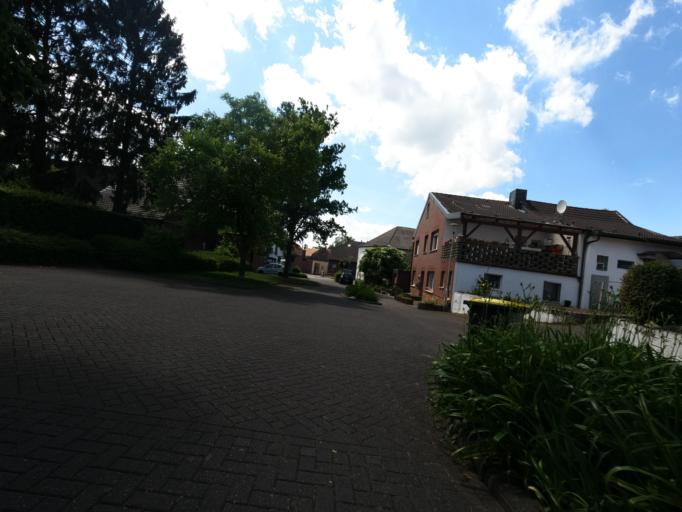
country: DE
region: North Rhine-Westphalia
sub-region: Regierungsbezirk Koln
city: Wassenberg
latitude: 51.0868
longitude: 6.1508
